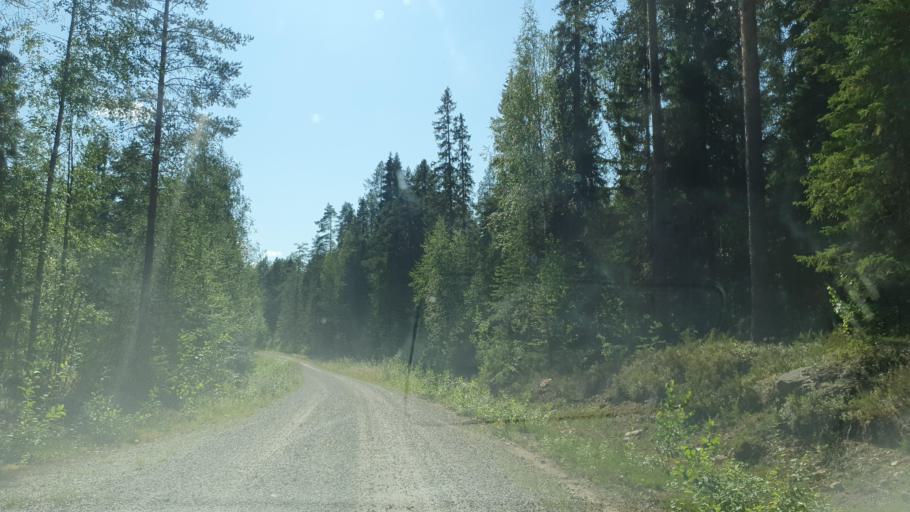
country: FI
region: Kainuu
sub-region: Kehys-Kainuu
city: Kuhmo
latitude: 63.9750
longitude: 29.5387
